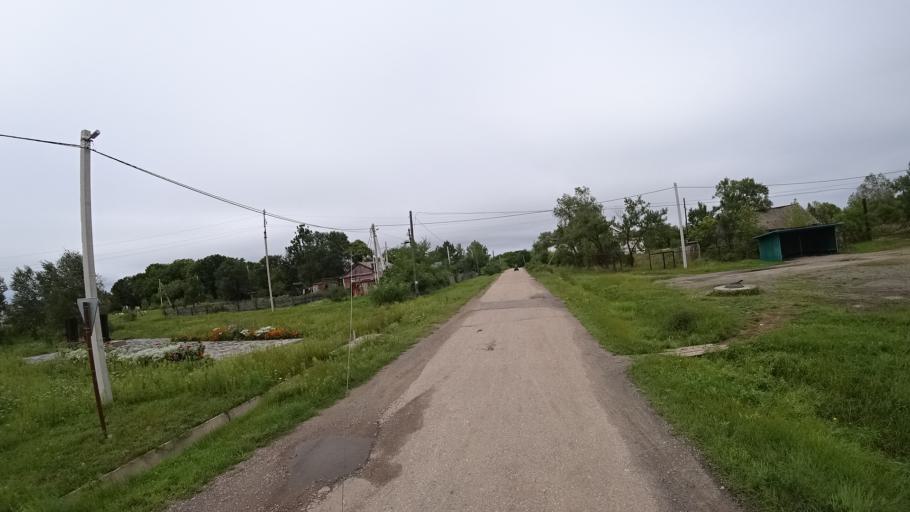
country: RU
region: Primorskiy
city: Monastyrishche
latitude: 44.0801
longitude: 132.5817
